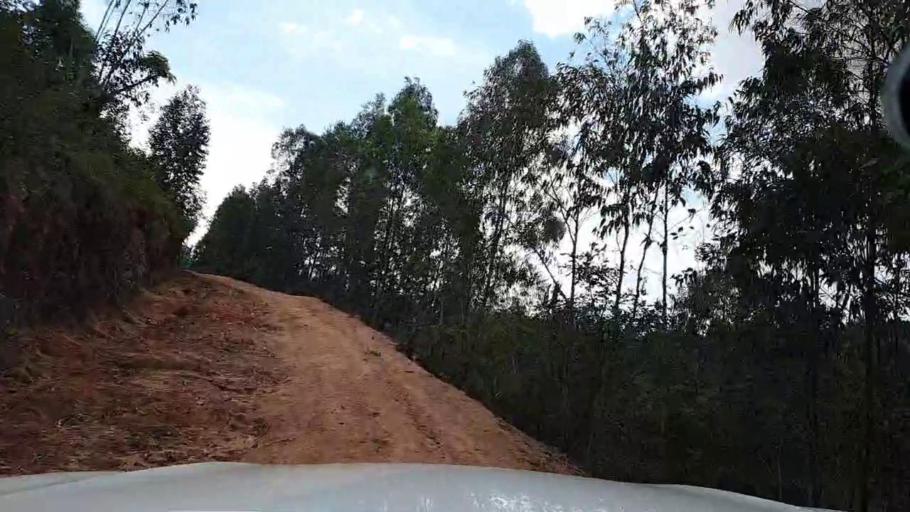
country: RW
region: Southern Province
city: Butare
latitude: -2.7465
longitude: 29.7633
